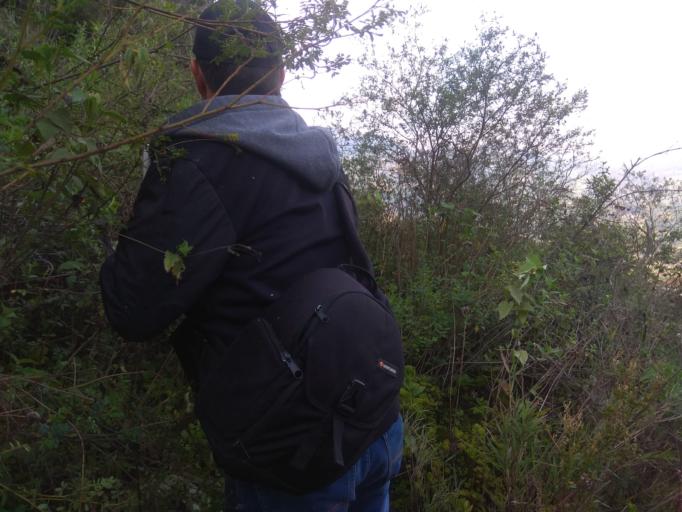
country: CO
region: Boyaca
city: Socha Viejo
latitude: 5.9910
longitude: -72.7014
